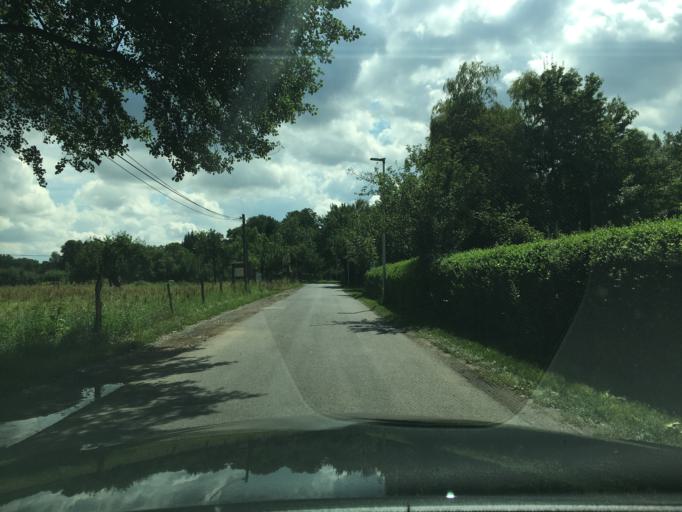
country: DE
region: Brandenburg
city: Burg
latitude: 51.8585
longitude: 14.1065
